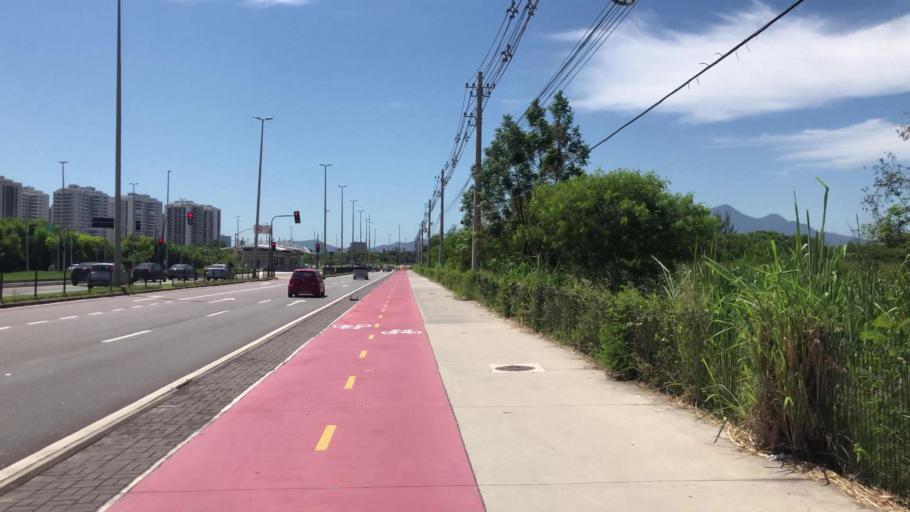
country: BR
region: Rio de Janeiro
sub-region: Nilopolis
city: Nilopolis
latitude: -22.9735
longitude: -43.3938
